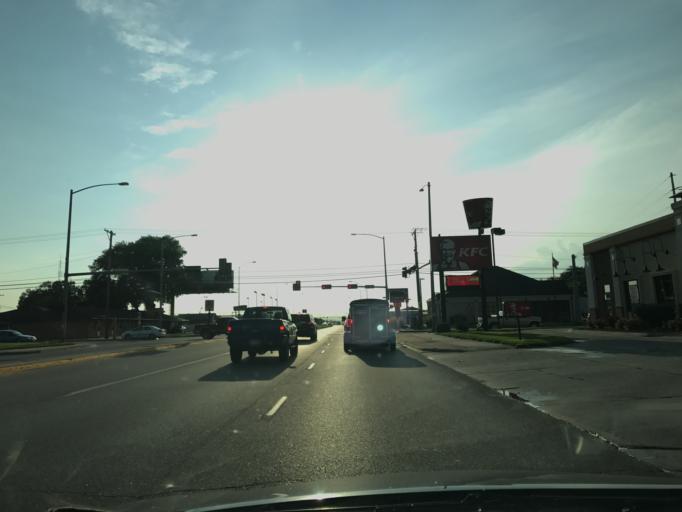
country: US
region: Nebraska
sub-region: Platte County
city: Columbus
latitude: 41.4385
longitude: -97.3499
